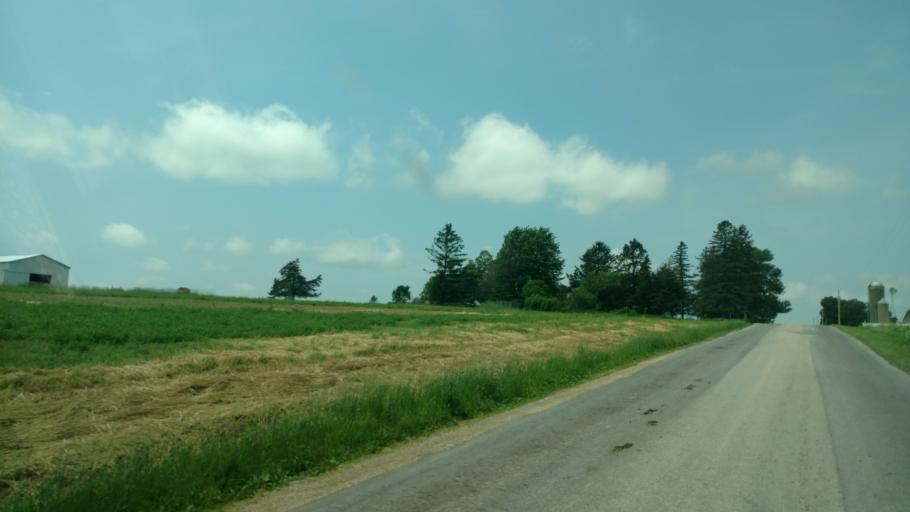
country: US
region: Wisconsin
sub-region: Monroe County
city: Cashton
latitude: 43.7146
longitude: -90.7124
